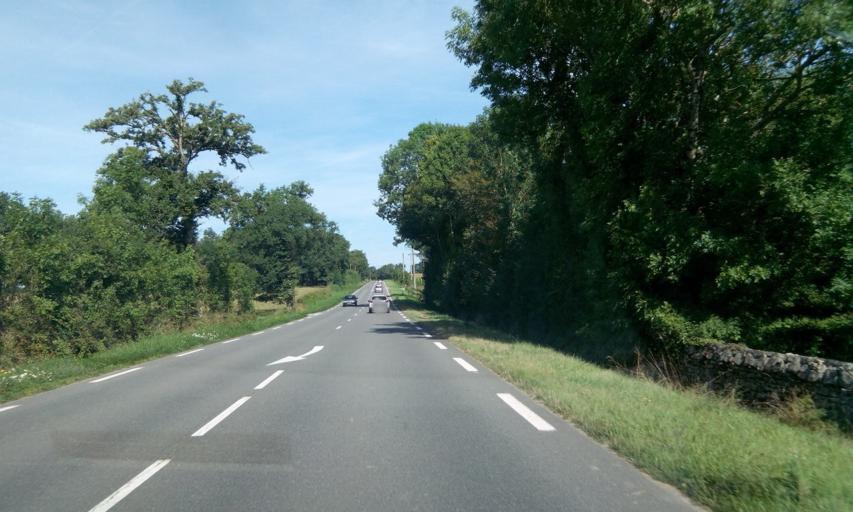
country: FR
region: Poitou-Charentes
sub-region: Departement de la Charente
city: Confolens
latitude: 46.0374
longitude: 0.6336
